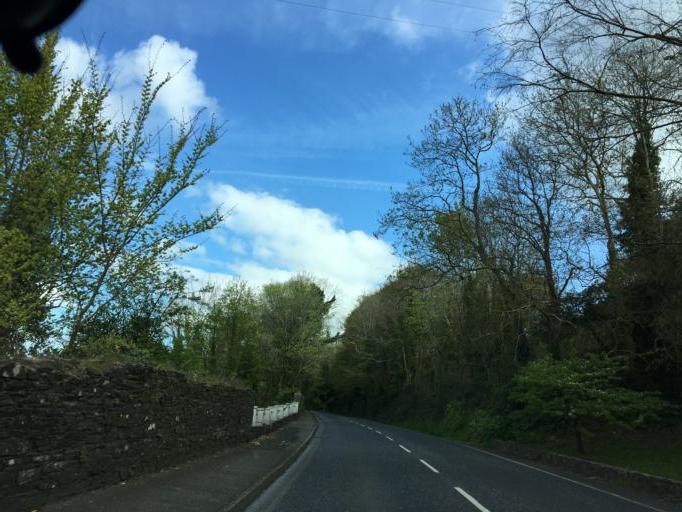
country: IE
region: Leinster
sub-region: Loch Garman
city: New Ross
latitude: 52.4009
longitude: -6.9399
